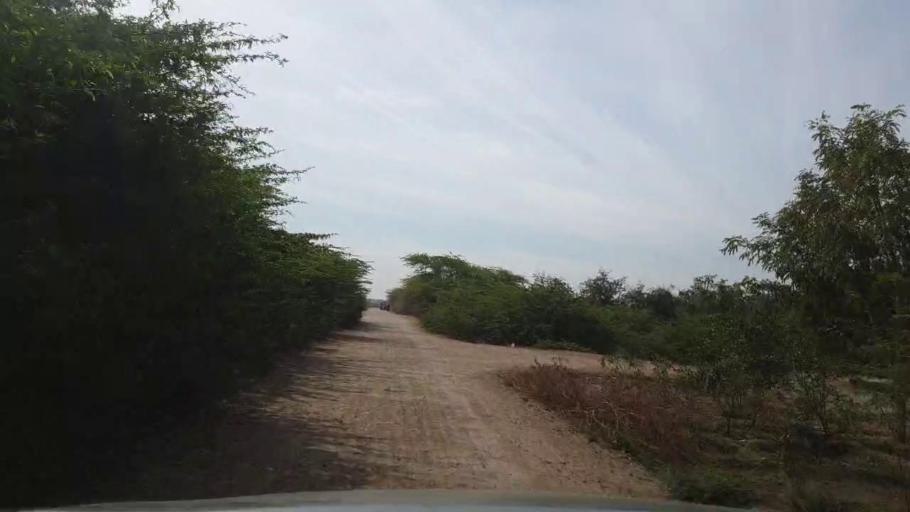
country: PK
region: Sindh
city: Kunri
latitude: 25.1476
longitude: 69.6044
